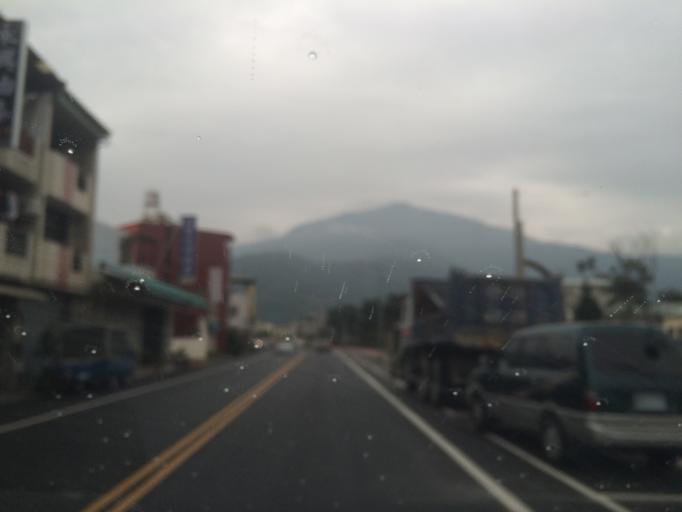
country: TW
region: Taiwan
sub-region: Nantou
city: Puli
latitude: 23.9563
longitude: 120.9709
